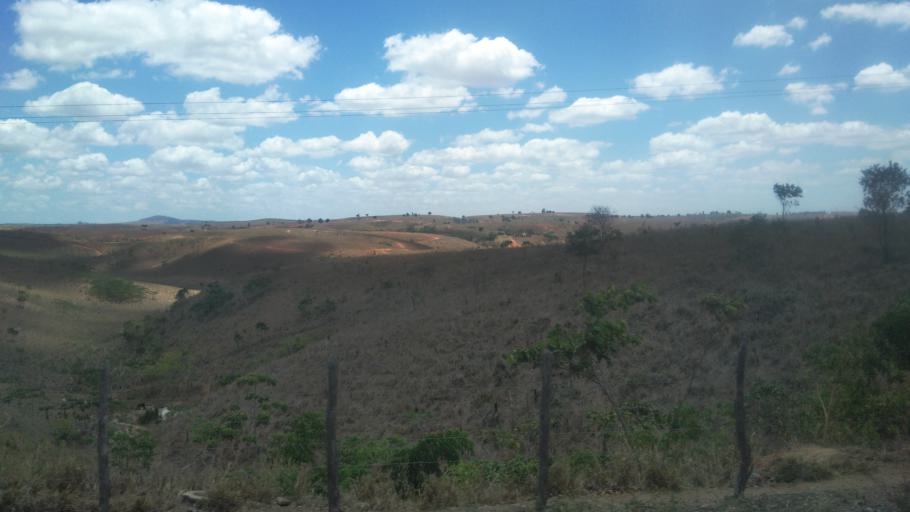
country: BR
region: Pernambuco
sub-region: Nazare Da Mata
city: Nazare da Mata
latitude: -7.7337
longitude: -35.2803
